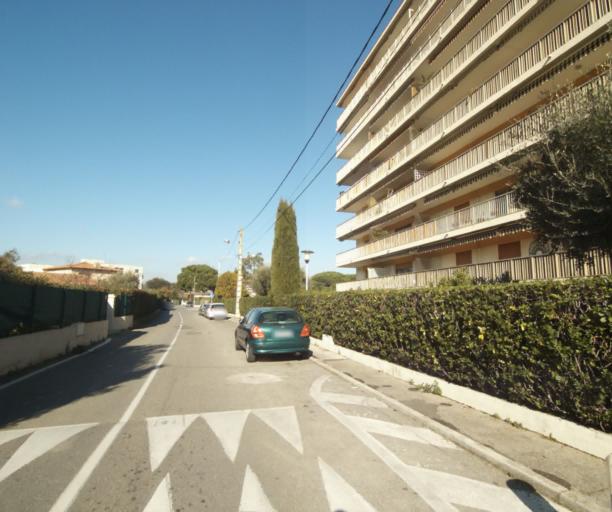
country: FR
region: Provence-Alpes-Cote d'Azur
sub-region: Departement des Alpes-Maritimes
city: Biot
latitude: 43.6084
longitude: 7.1182
